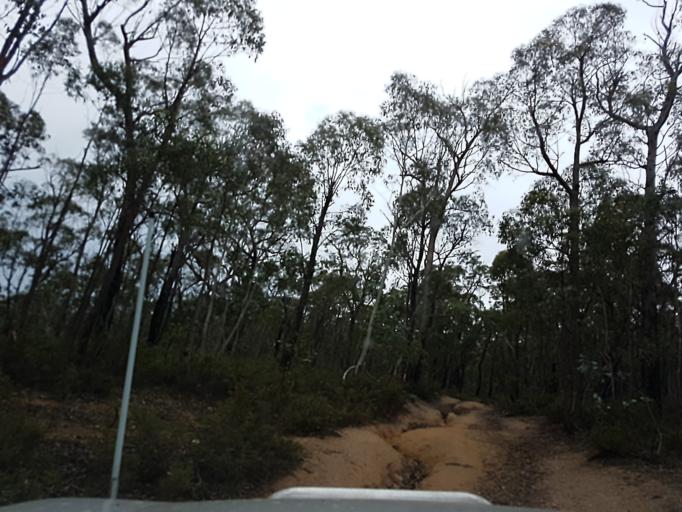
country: AU
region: New South Wales
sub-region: Snowy River
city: Jindabyne
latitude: -36.8608
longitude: 148.3278
